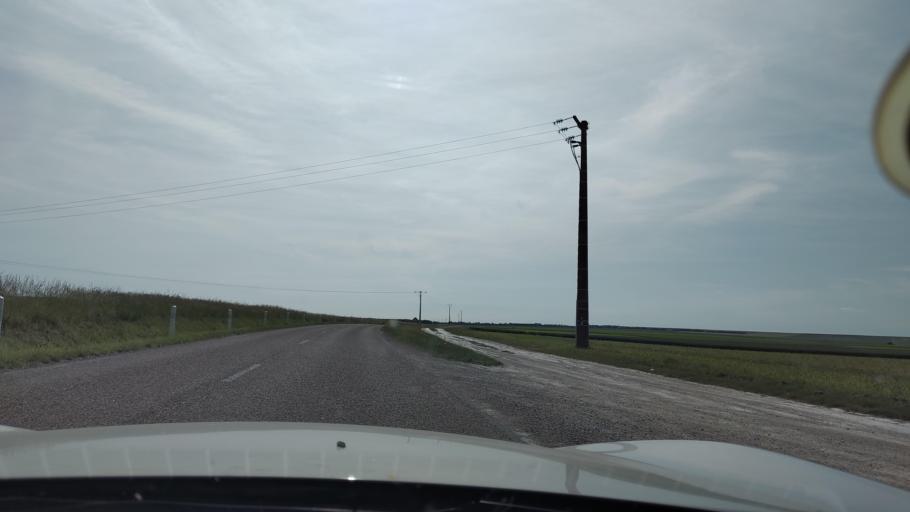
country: FR
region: Champagne-Ardenne
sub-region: Departement de l'Aube
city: Marigny-le-Chatel
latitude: 48.4023
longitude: 3.7659
